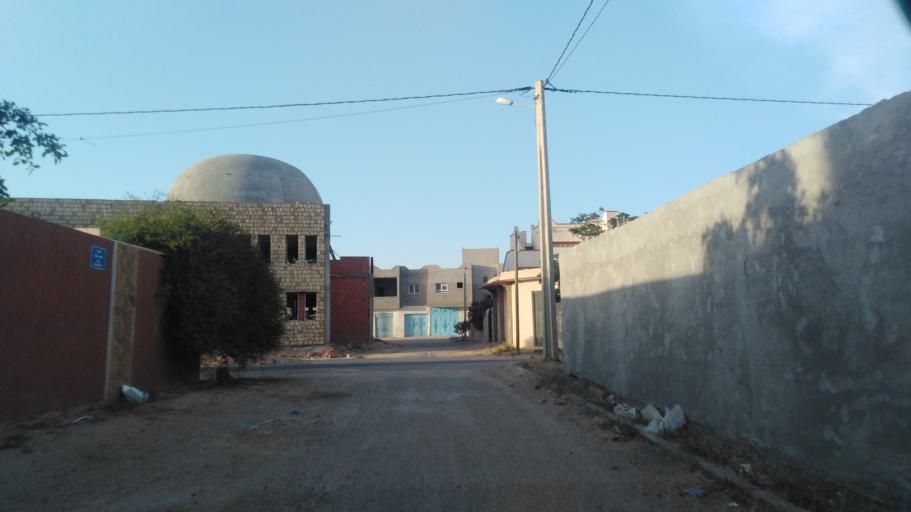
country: TN
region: Tataouine
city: Tataouine
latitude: 32.9531
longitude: 10.4650
